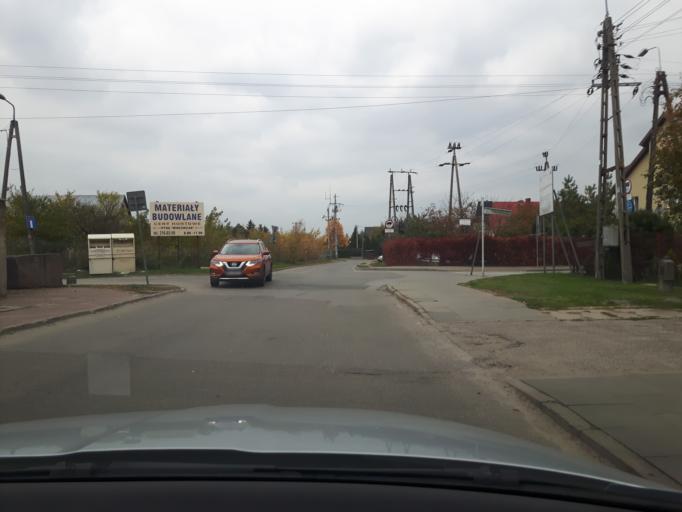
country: PL
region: Masovian Voivodeship
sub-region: Powiat wolominski
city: Zabki
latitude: 52.2879
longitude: 21.0950
